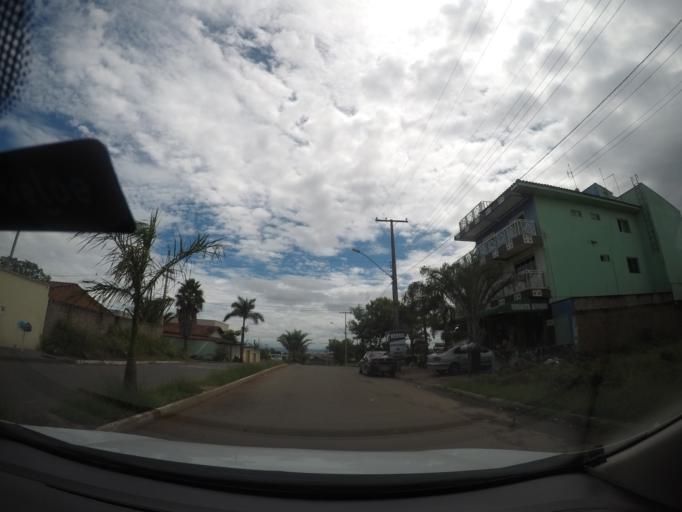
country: BR
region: Goias
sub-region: Goiania
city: Goiania
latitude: -16.7554
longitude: -49.3500
